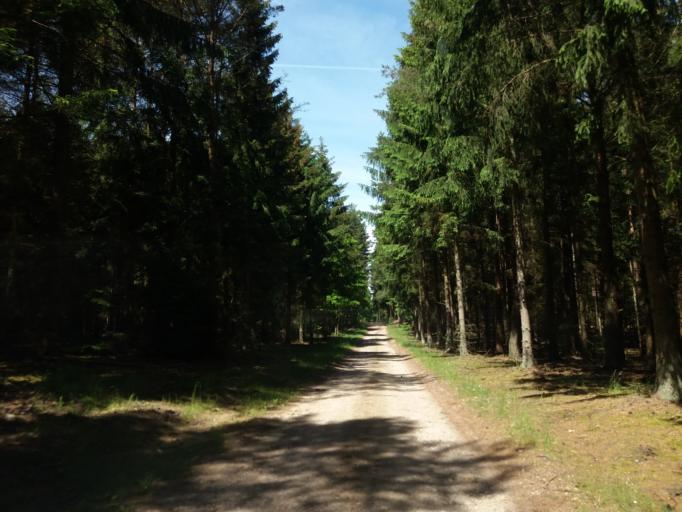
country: PL
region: West Pomeranian Voivodeship
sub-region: Powiat choszczenski
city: Recz
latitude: 53.3299
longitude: 15.5258
